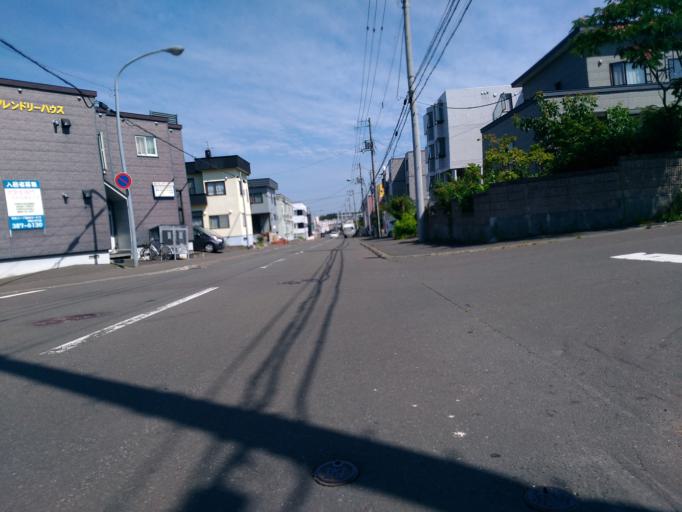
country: JP
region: Hokkaido
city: Ebetsu
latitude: 43.0668
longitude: 141.4984
